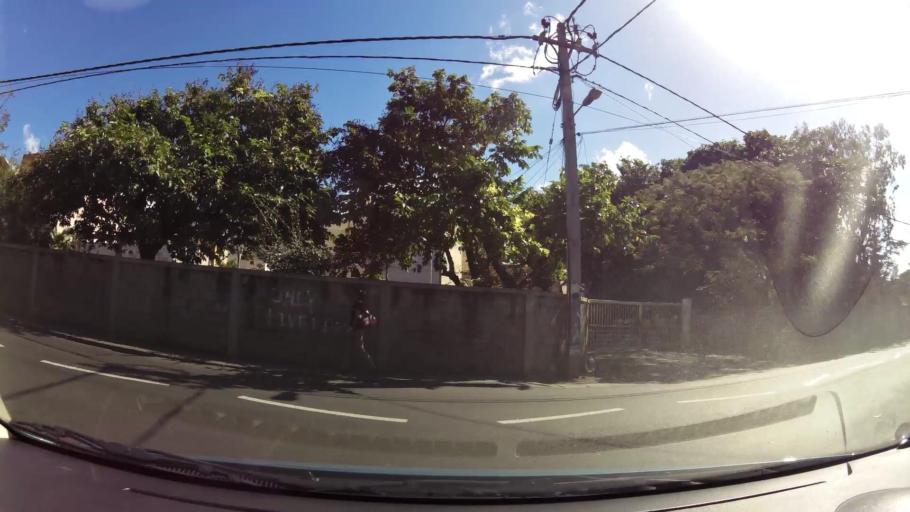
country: MU
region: Black River
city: Cascavelle
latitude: -20.2580
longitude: 57.4177
